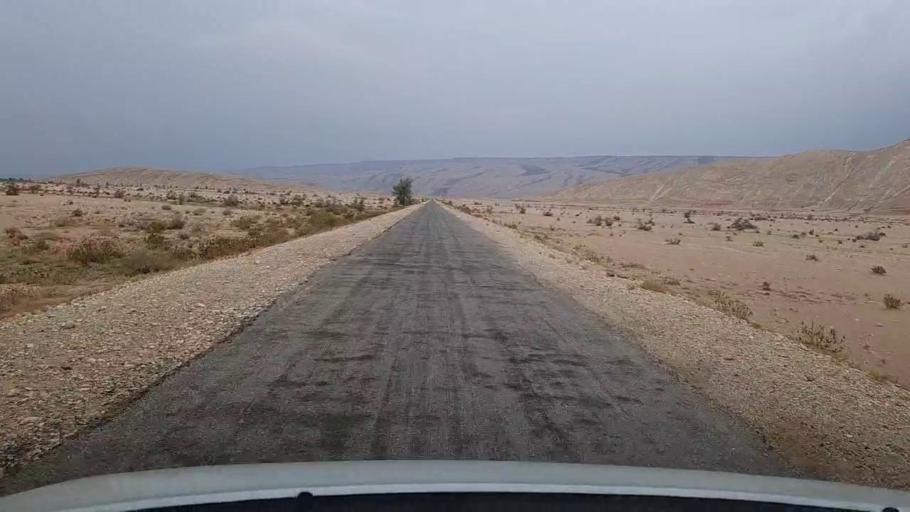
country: PK
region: Sindh
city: Sehwan
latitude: 26.2409
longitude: 67.7133
